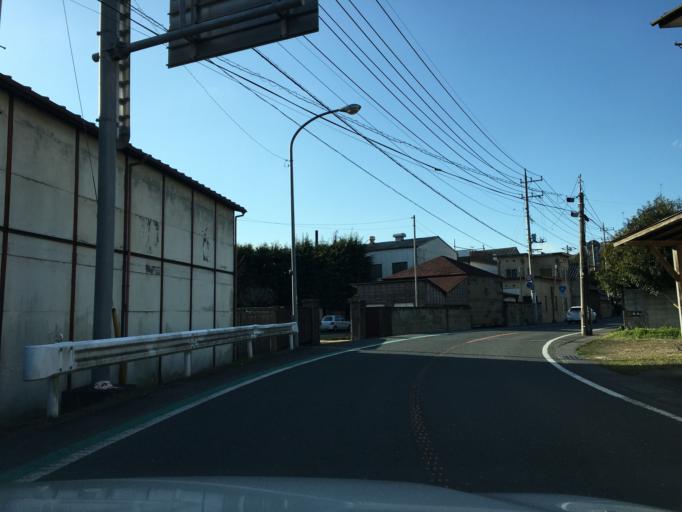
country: JP
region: Ibaraki
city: Daigo
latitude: 36.7759
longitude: 140.3469
